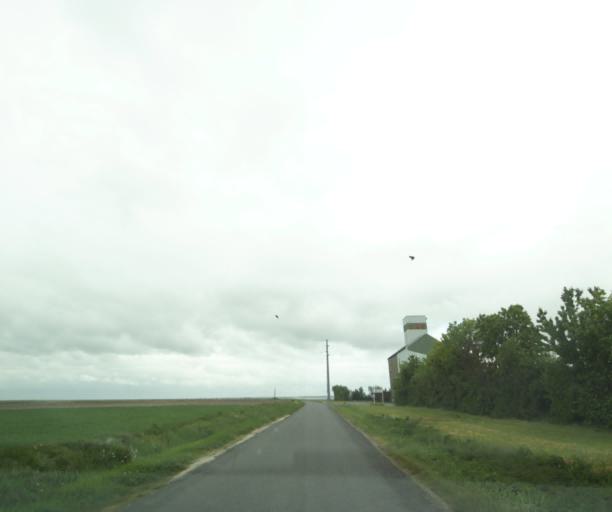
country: FR
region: Poitou-Charentes
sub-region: Departement de la Charente-Maritime
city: Perignac
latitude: 45.6598
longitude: -0.5050
